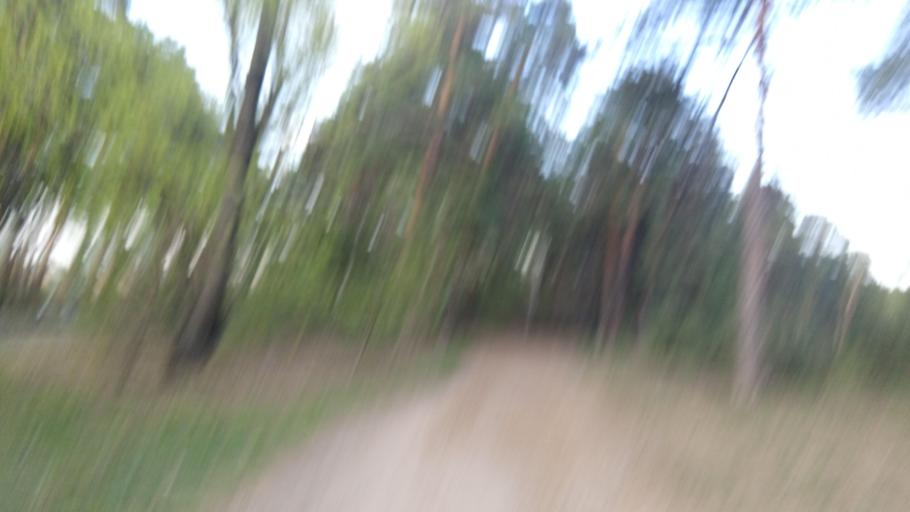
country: RU
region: Chelyabinsk
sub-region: Gorod Chelyabinsk
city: Chelyabinsk
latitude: 55.1674
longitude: 61.3443
